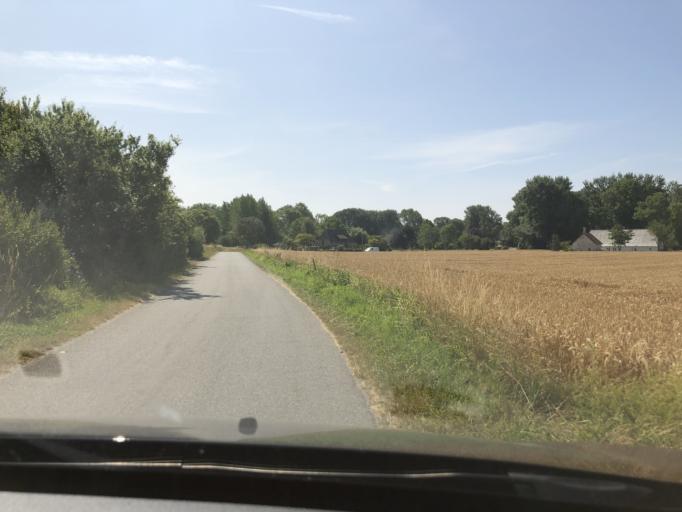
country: DK
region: South Denmark
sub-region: AEro Kommune
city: AEroskobing
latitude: 54.9177
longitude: 10.2952
